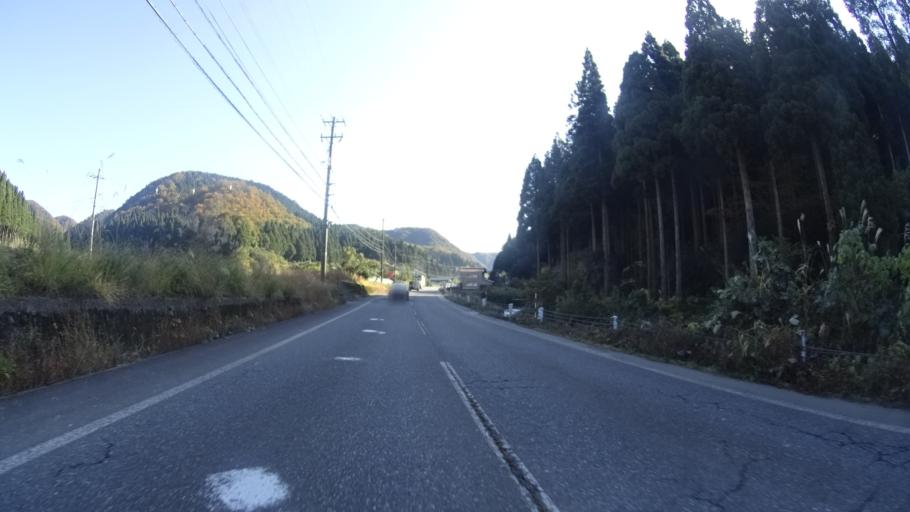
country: JP
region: Ishikawa
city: Komatsu
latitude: 36.3746
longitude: 136.5460
